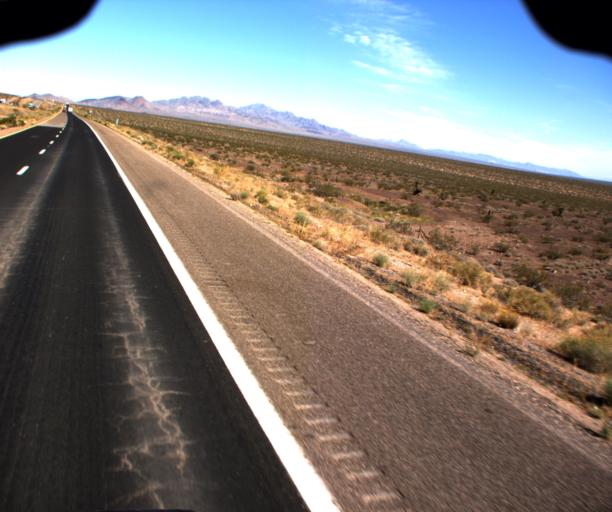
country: US
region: Arizona
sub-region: Mohave County
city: Dolan Springs
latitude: 35.7858
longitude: -114.5218
